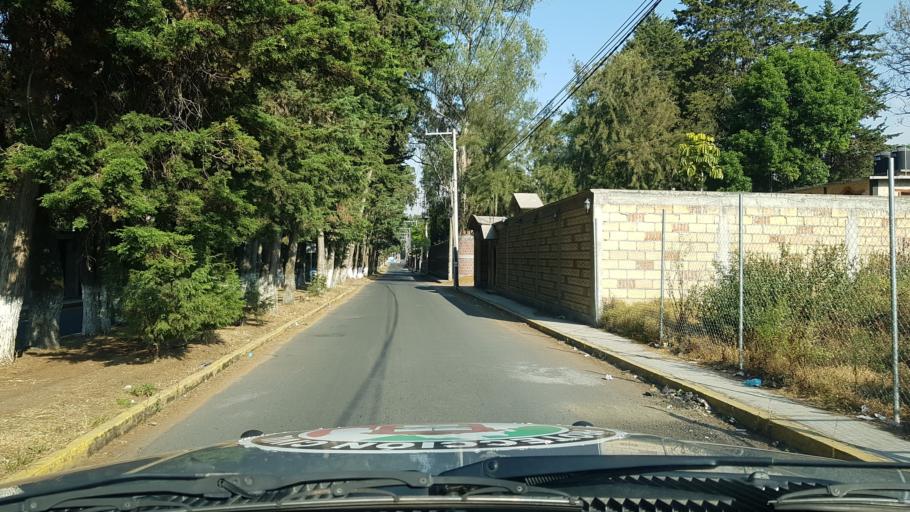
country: MX
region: Mexico
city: Ozumba de Alzate
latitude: 19.0620
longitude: -98.7821
